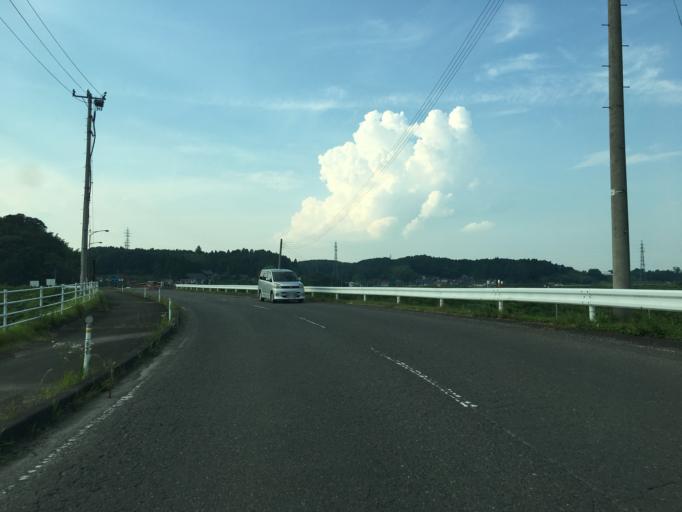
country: JP
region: Fukushima
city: Nihommatsu
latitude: 37.5622
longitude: 140.4353
